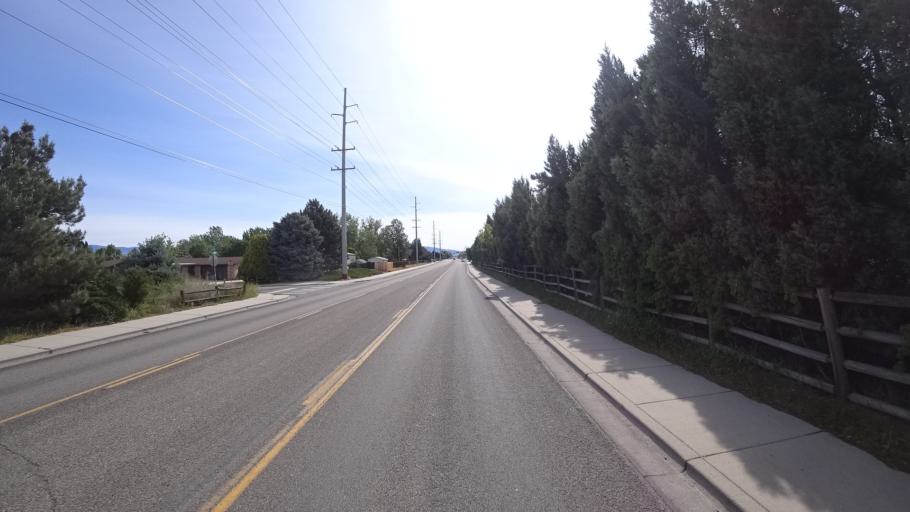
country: US
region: Idaho
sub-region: Ada County
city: Garden City
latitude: 43.5757
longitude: -116.2991
